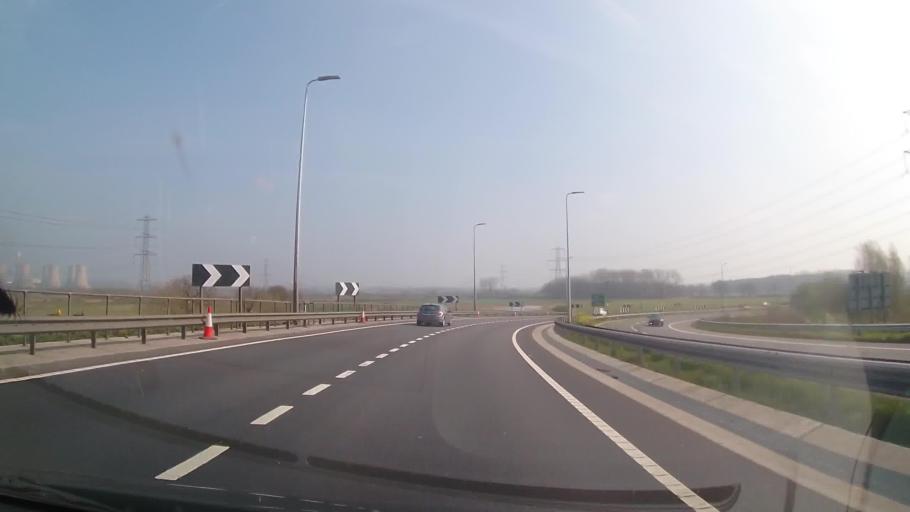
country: GB
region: England
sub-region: Leicestershire
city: Kegworth
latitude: 52.8553
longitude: -1.2968
